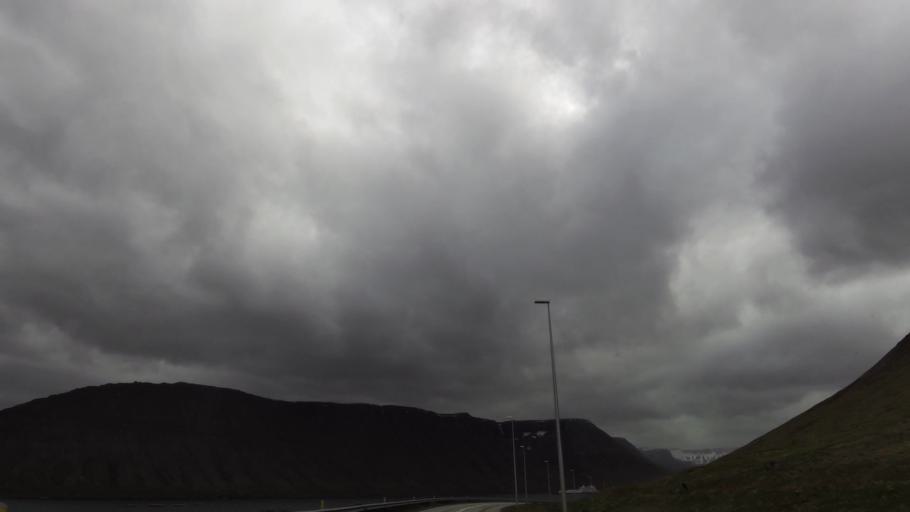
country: IS
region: Westfjords
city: Isafjoerdur
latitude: 66.1007
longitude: -23.1094
